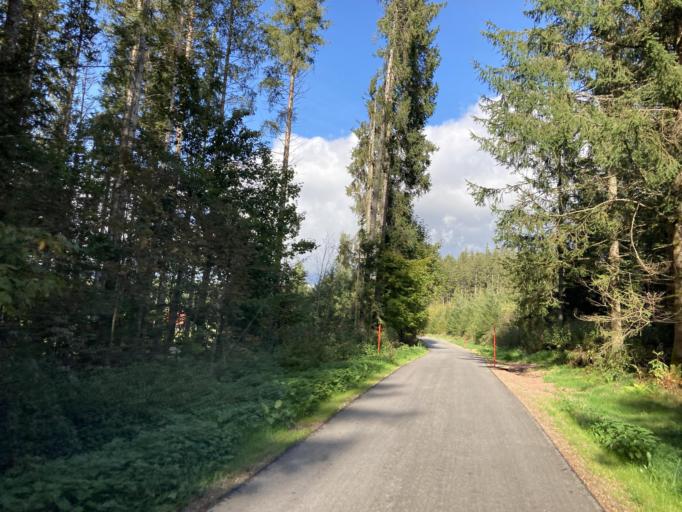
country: DE
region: Baden-Wuerttemberg
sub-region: Freiburg Region
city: Vohrenbach
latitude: 48.0835
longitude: 8.2782
